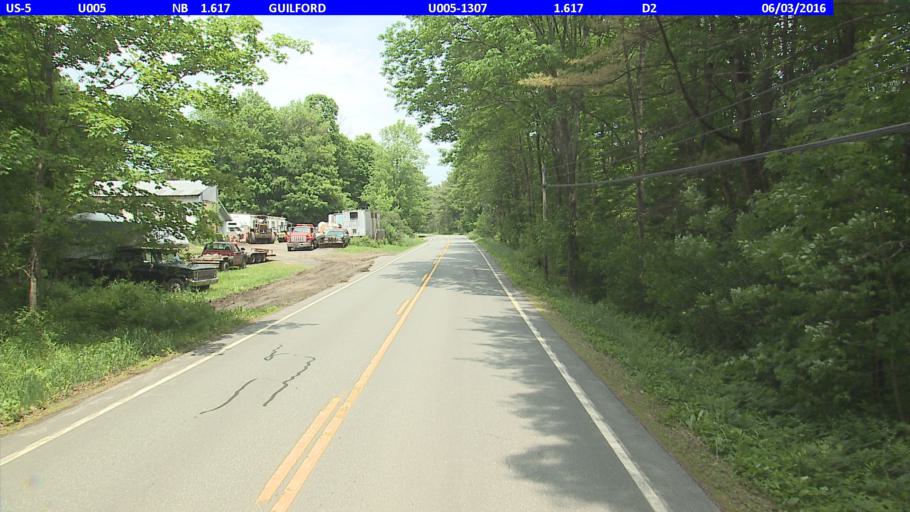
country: US
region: Massachusetts
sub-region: Franklin County
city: Bernardston
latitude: 42.7528
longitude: -72.5692
